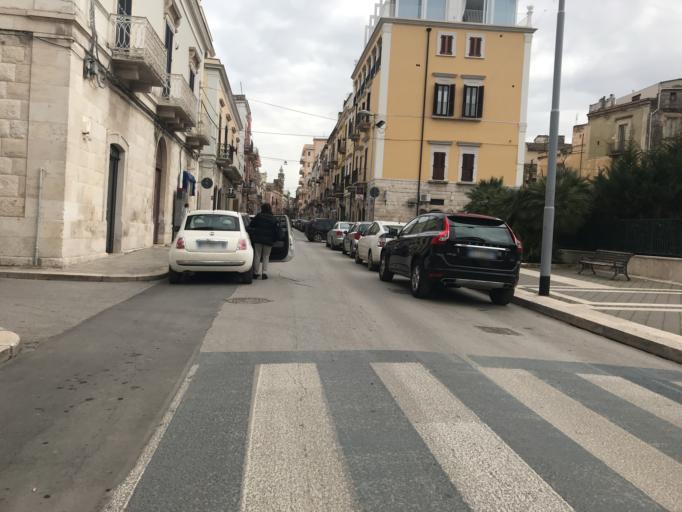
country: IT
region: Apulia
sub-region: Provincia di Bari
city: Corato
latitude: 41.1563
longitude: 16.4117
